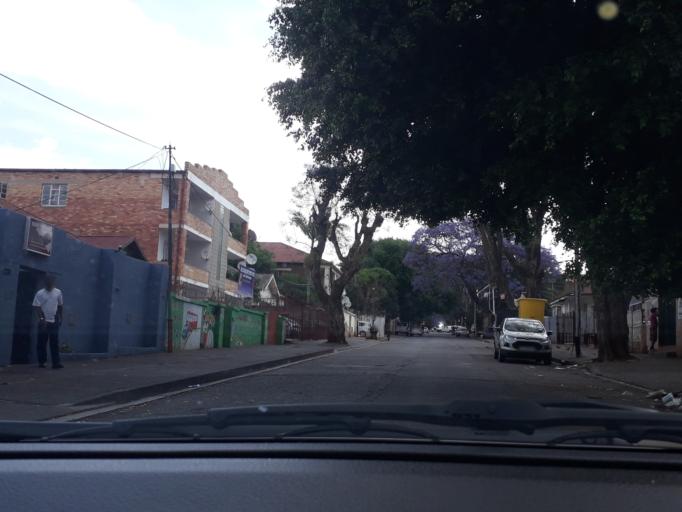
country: ZA
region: Gauteng
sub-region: City of Johannesburg Metropolitan Municipality
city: Johannesburg
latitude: -26.1791
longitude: 28.0718
